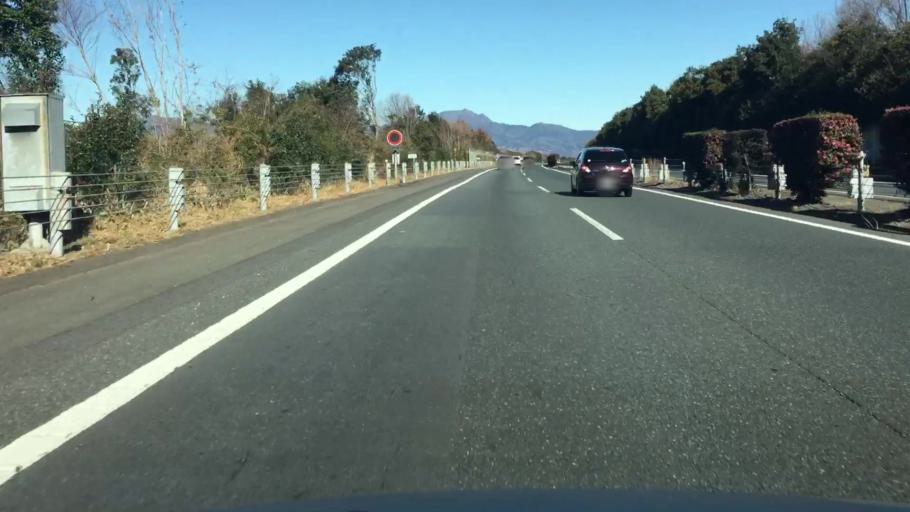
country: JP
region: Gunma
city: Kanekomachi
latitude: 36.4356
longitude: 139.0143
